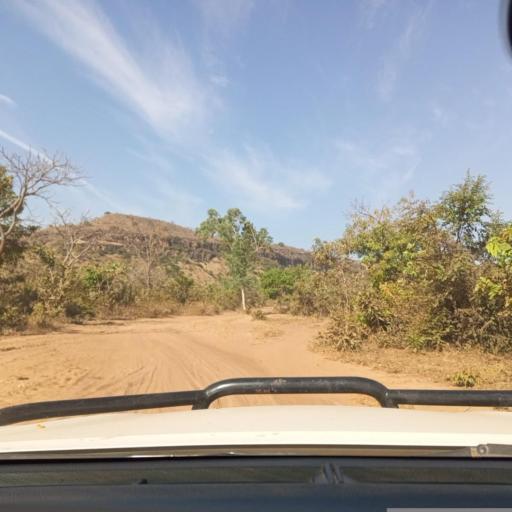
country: ML
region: Bamako
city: Bamako
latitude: 12.5568
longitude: -8.1482
